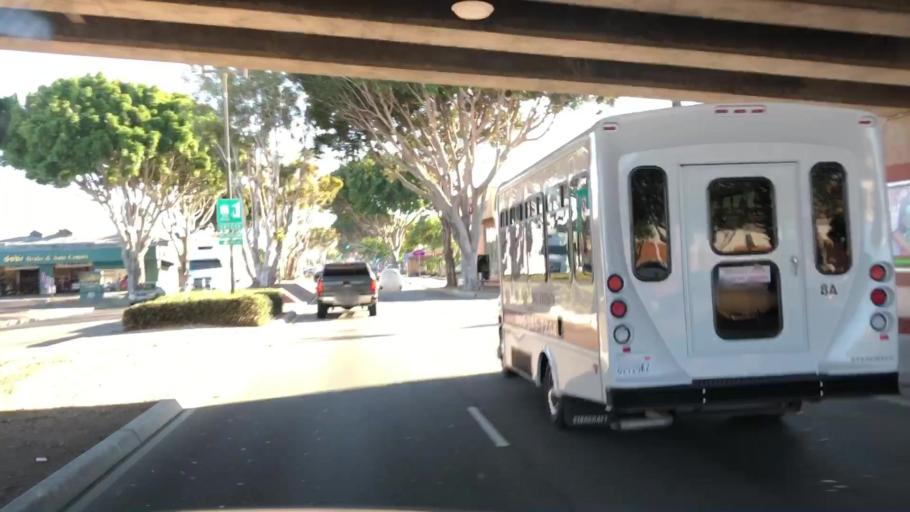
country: US
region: California
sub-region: Ventura County
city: Oxnard
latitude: 34.2004
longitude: -119.1774
